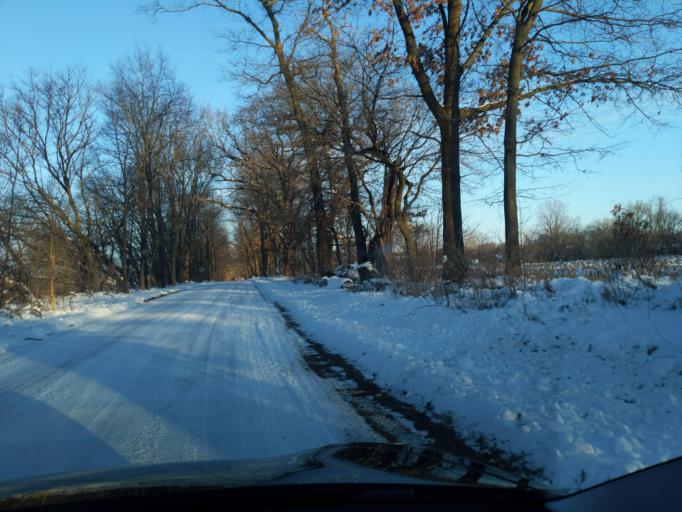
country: US
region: Michigan
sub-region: Ingham County
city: Stockbridge
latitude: 42.5343
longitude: -84.1170
